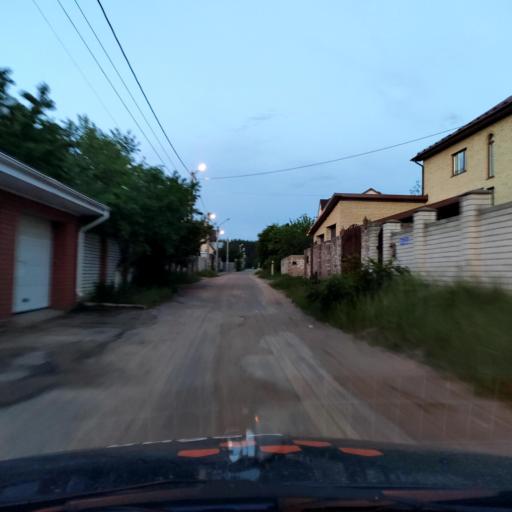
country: RU
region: Voronezj
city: Podgornoye
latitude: 51.7468
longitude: 39.1547
